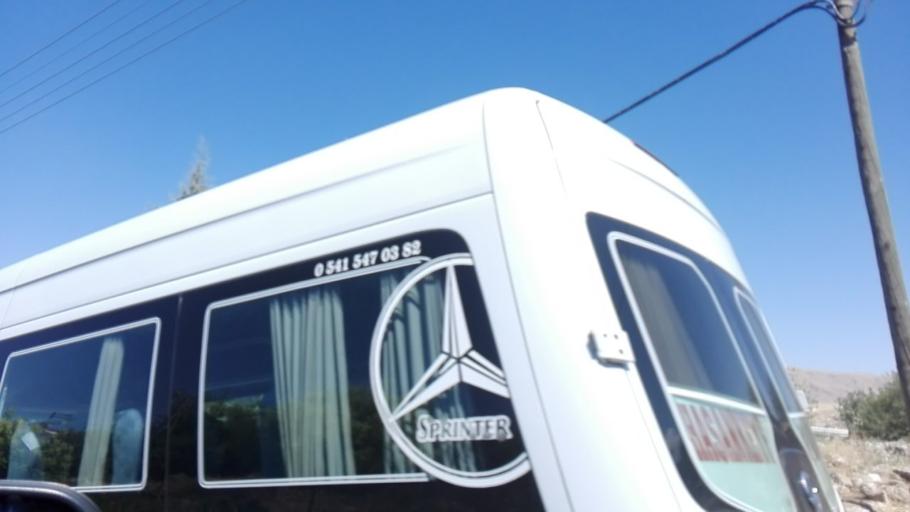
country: TR
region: Batman
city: Hasankeyf
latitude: 37.7135
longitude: 41.4139
